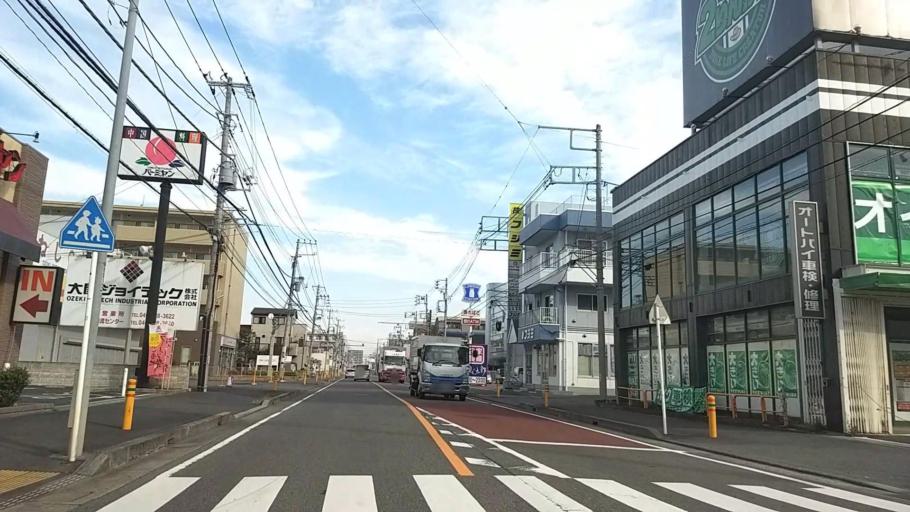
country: JP
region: Kanagawa
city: Atsugi
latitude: 35.4240
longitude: 139.3653
